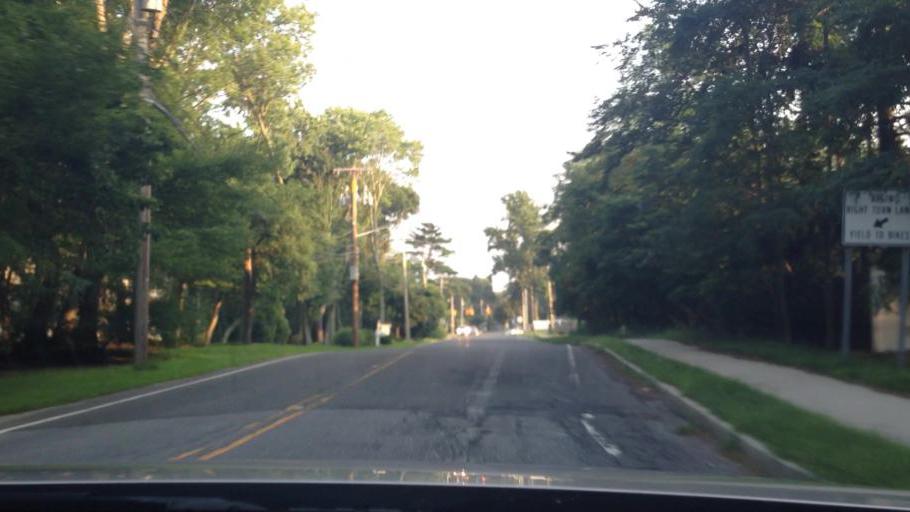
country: US
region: New York
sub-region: Suffolk County
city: Holtsville
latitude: 40.8380
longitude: -73.0543
